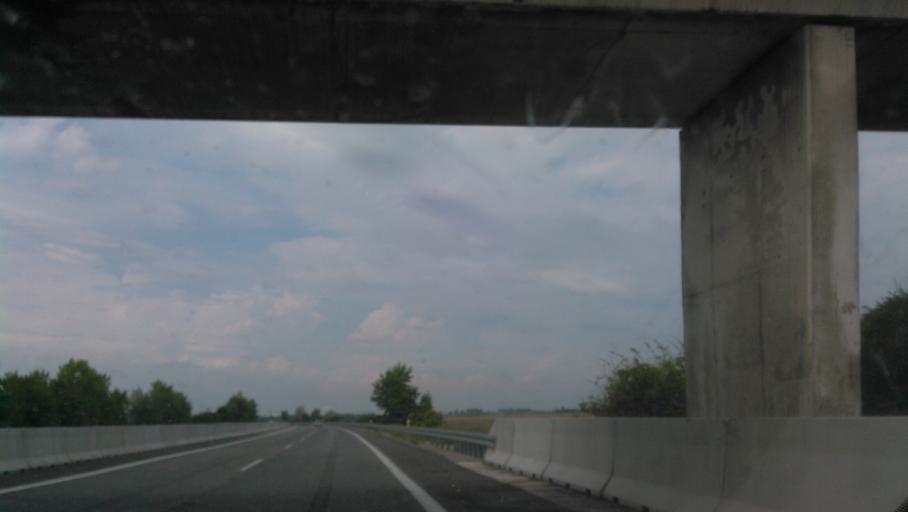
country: SK
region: Trnavsky
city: Leopoldov
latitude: 48.4064
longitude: 17.7482
